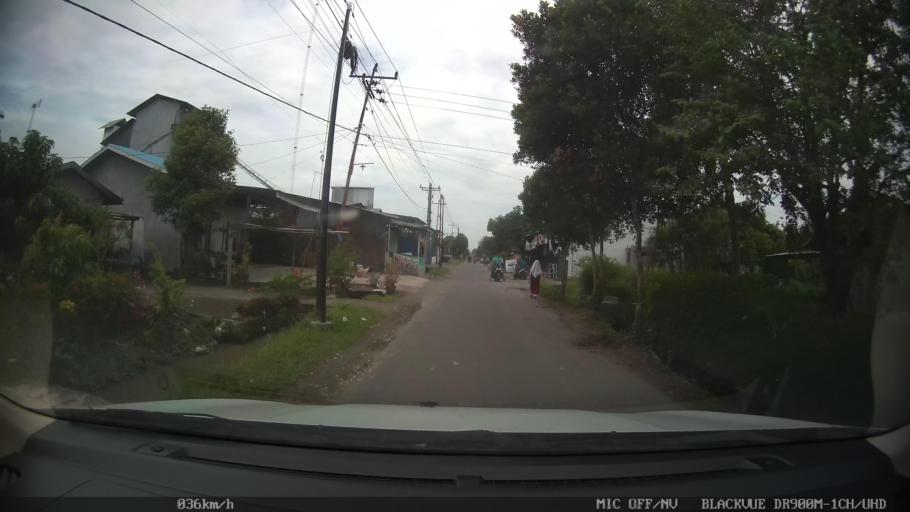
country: ID
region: North Sumatra
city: Binjai
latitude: 3.6292
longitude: 98.5574
